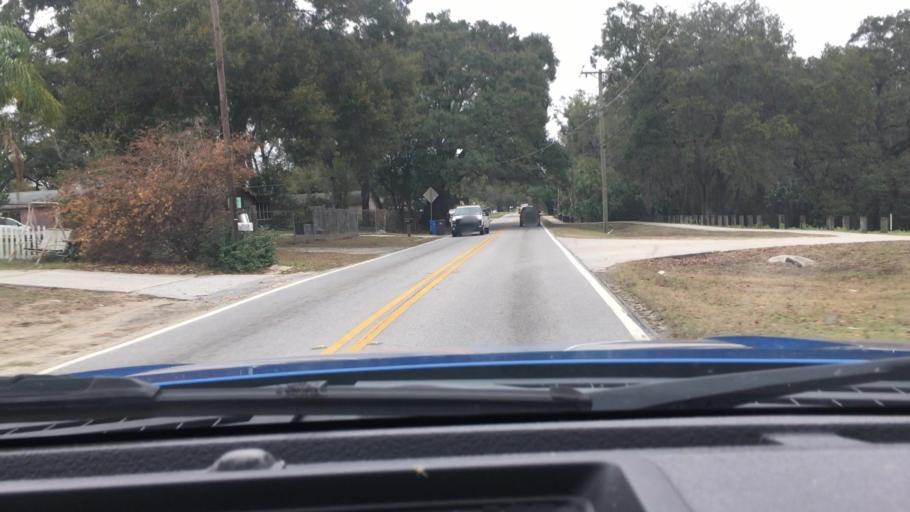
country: US
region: Florida
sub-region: Hillsborough County
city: Mango
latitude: 27.9606
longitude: -82.3104
